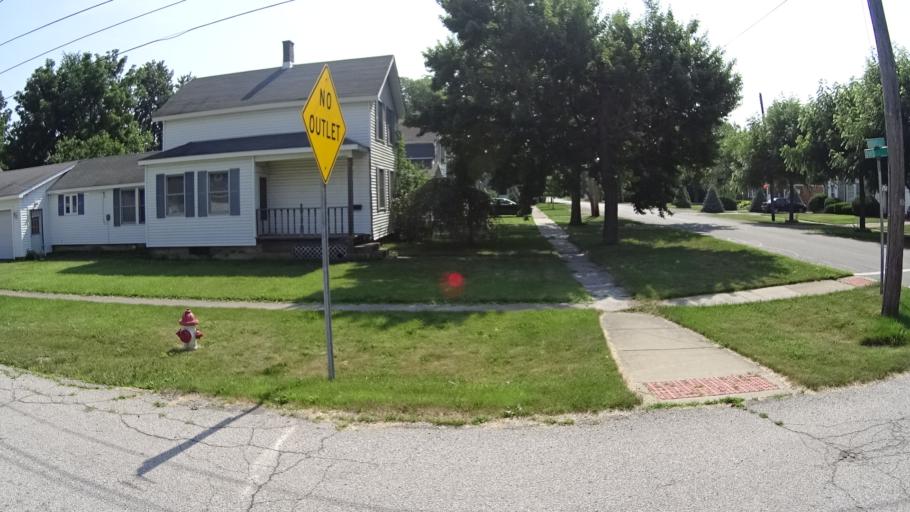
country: US
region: Ohio
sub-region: Lorain County
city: Vermilion
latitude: 41.4202
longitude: -82.3685
